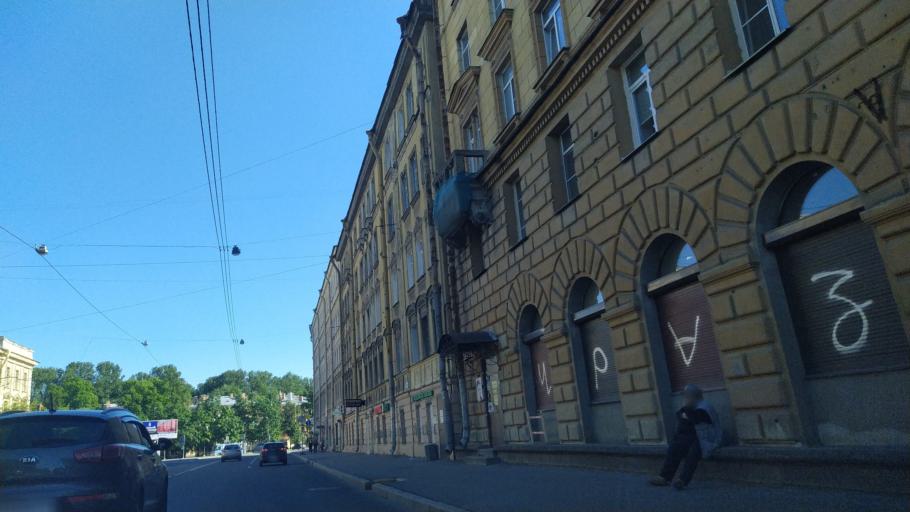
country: RU
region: Leningrad
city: Finlyandskiy
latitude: 59.9607
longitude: 30.3450
